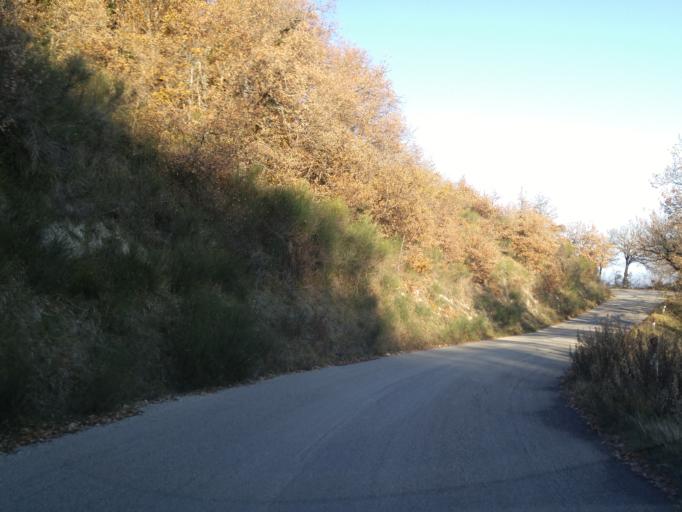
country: IT
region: The Marches
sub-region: Provincia di Pesaro e Urbino
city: Montefelcino
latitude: 43.7639
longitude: 12.8278
